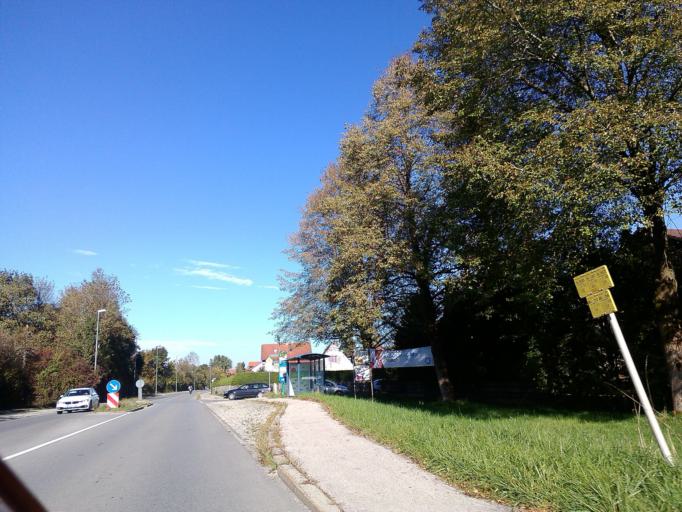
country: DE
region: Bavaria
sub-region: Upper Bavaria
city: Gauting
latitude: 48.0618
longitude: 11.3745
